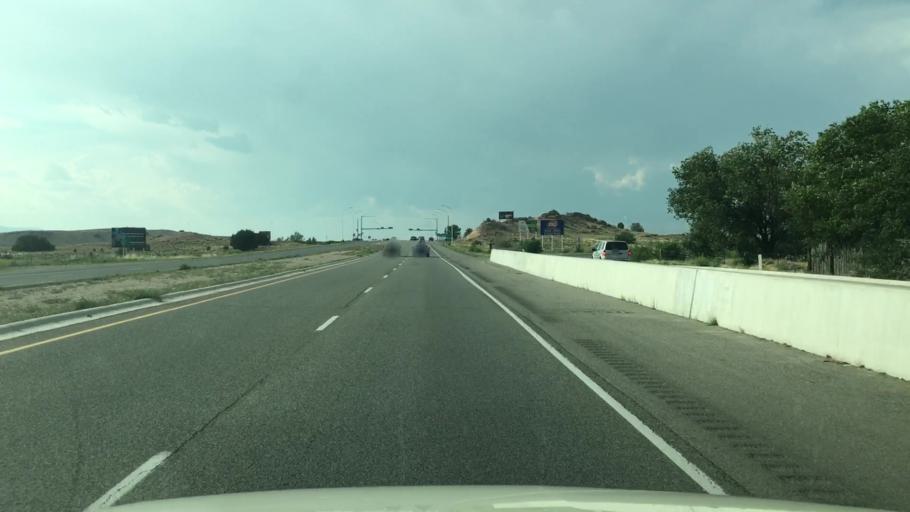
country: US
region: New Mexico
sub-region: Santa Fe County
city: El Valle de Arroyo Seco
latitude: 35.9729
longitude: -106.0413
